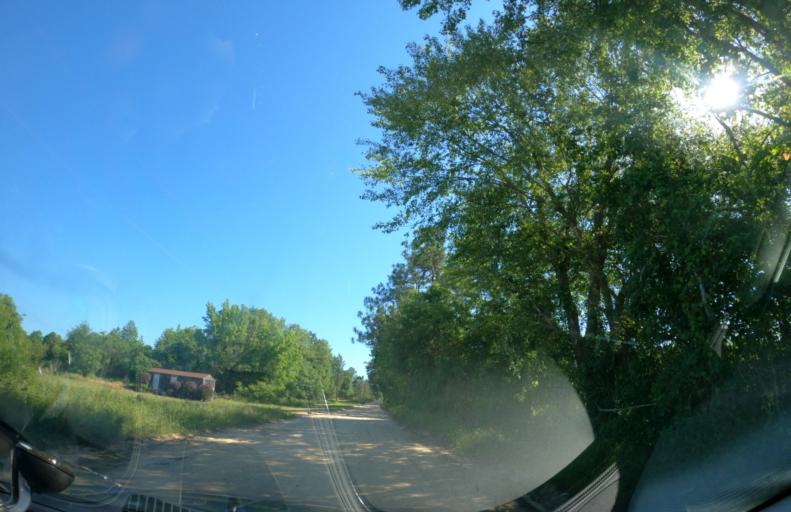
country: US
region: Georgia
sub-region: Jefferson County
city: Wrens
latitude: 33.2172
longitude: -82.3569
